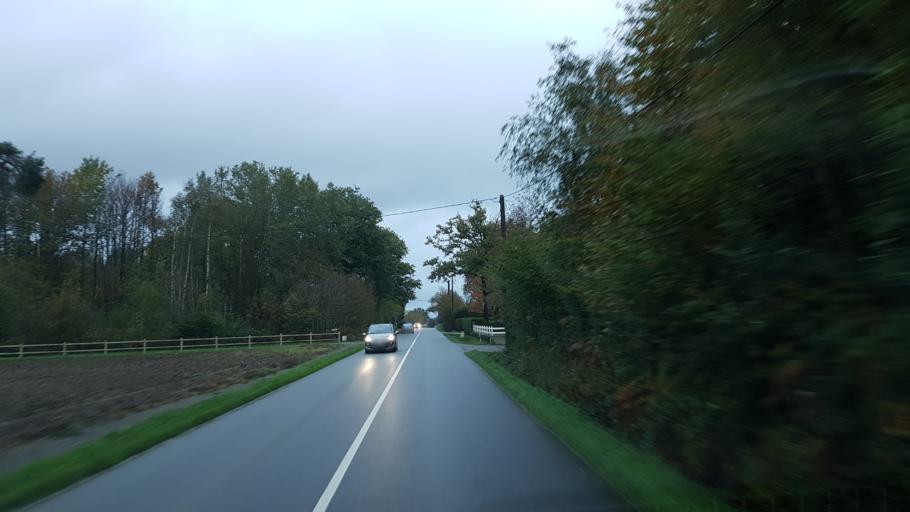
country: FR
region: Brittany
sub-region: Departement d'Ille-et-Vilaine
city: Balaze
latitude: 48.1559
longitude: -1.1428
